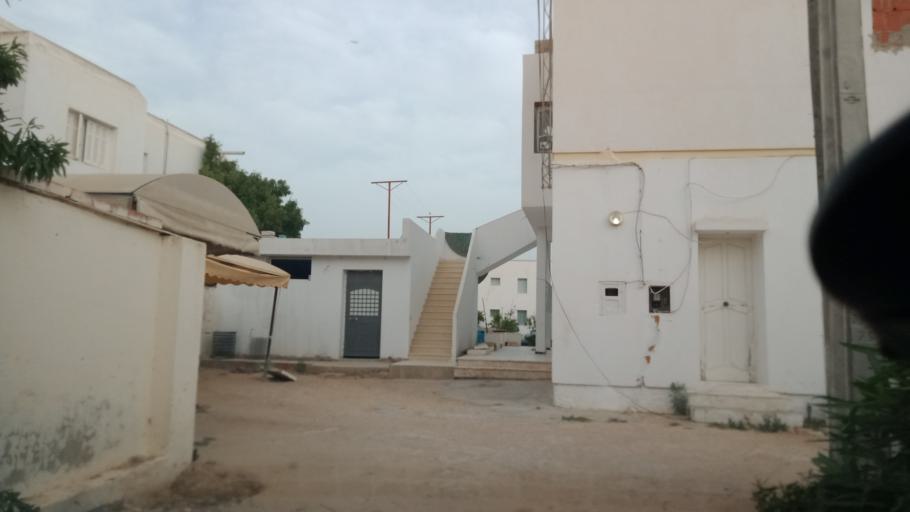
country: TN
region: Safaqis
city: Al Qarmadah
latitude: 34.7869
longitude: 10.7624
